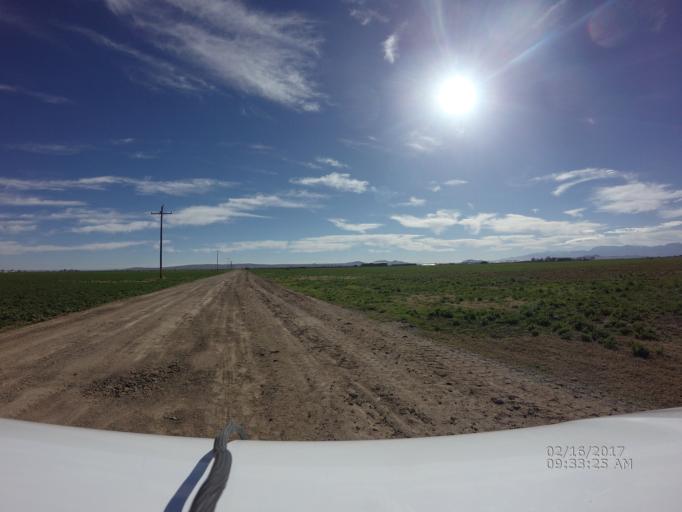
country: US
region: California
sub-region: Kern County
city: Edwards Air Force Base
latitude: 34.7488
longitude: -117.9603
